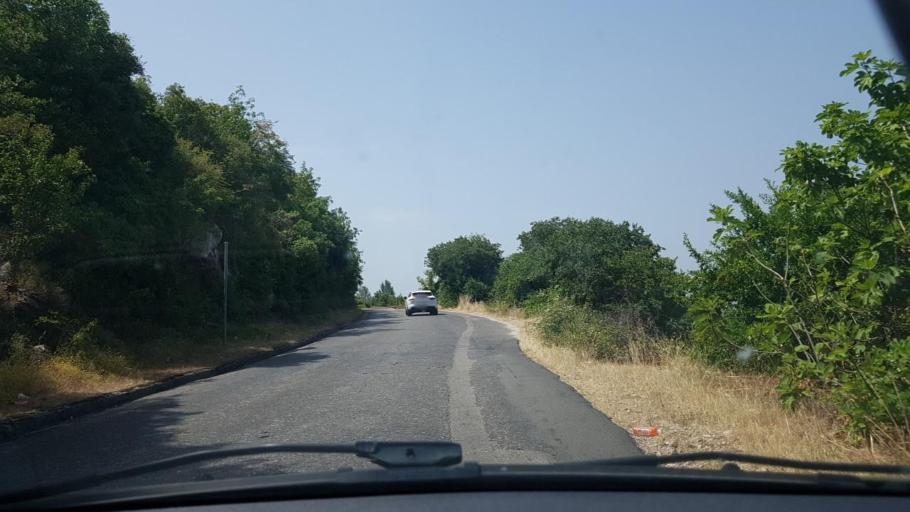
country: BA
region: Federation of Bosnia and Herzegovina
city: Tasovcici
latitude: 43.0193
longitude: 17.7688
